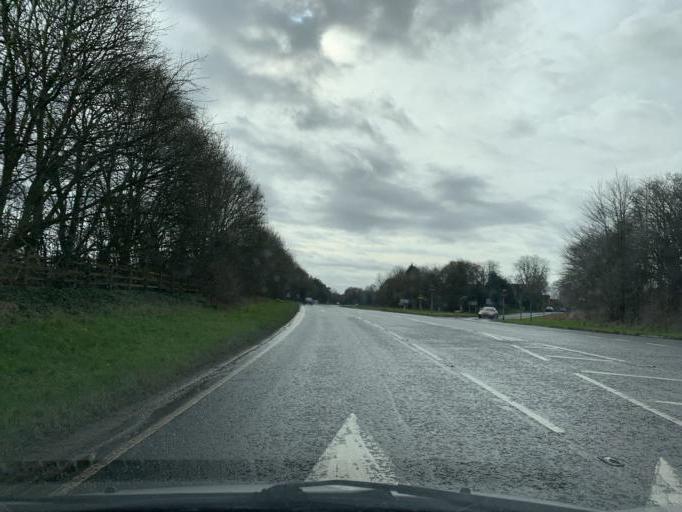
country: GB
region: England
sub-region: Hampshire
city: Fordingbridge
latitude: 50.9375
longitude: -1.7851
